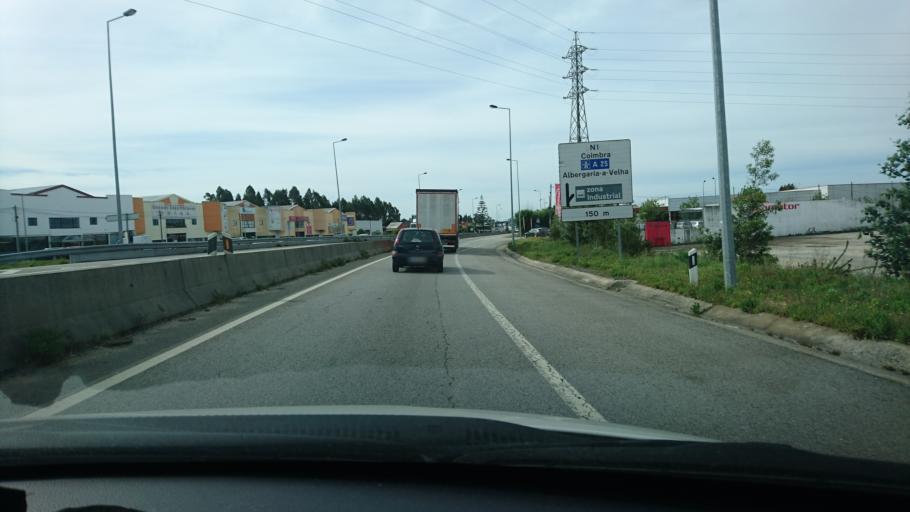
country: PT
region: Aveiro
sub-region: Albergaria-A-Velha
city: Albergaria-a-Velha
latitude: 40.7112
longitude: -8.4827
